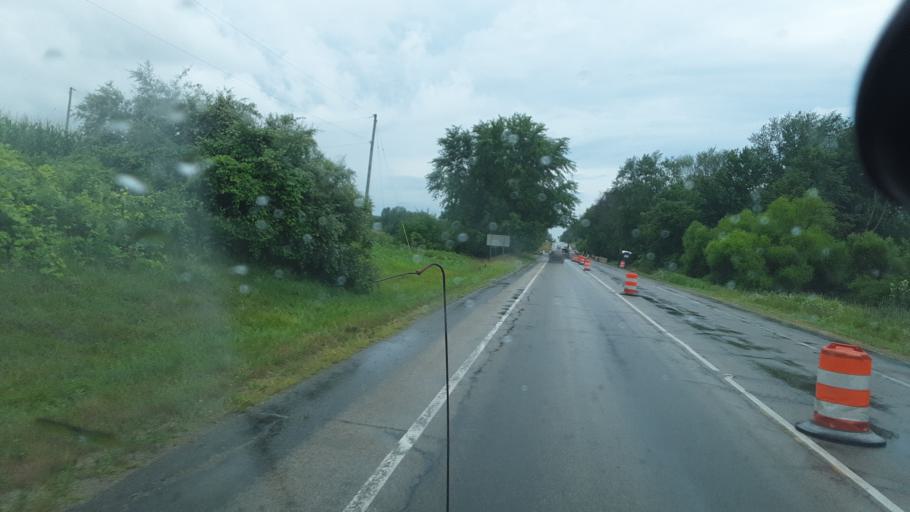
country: US
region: Indiana
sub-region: Steuben County
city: Hamilton
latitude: 41.6305
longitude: -84.8224
